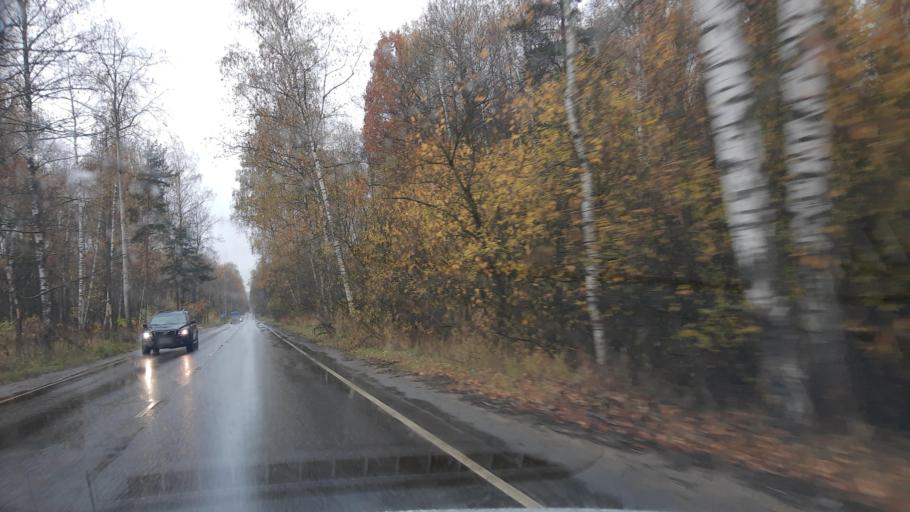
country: RU
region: Moskovskaya
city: Elektrostal'
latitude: 55.8000
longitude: 38.3769
